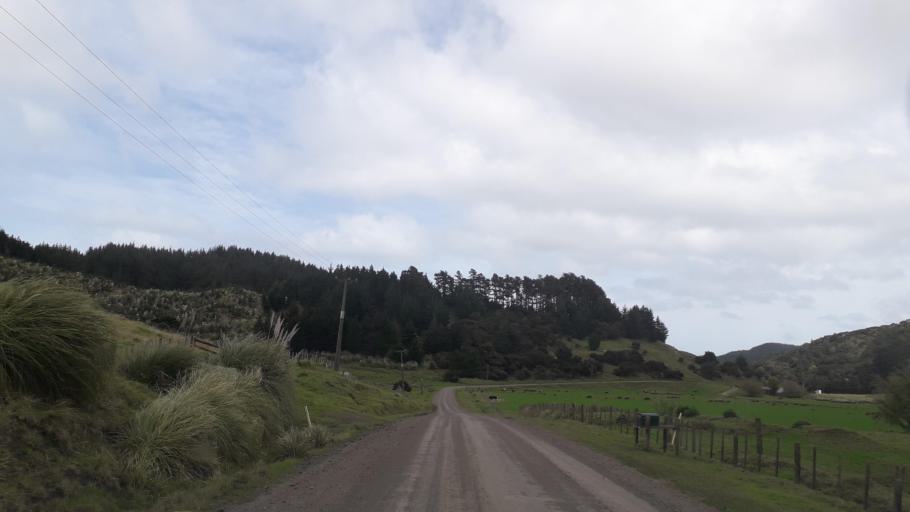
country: NZ
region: Northland
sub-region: Far North District
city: Ahipara
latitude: -35.4386
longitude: 173.3279
